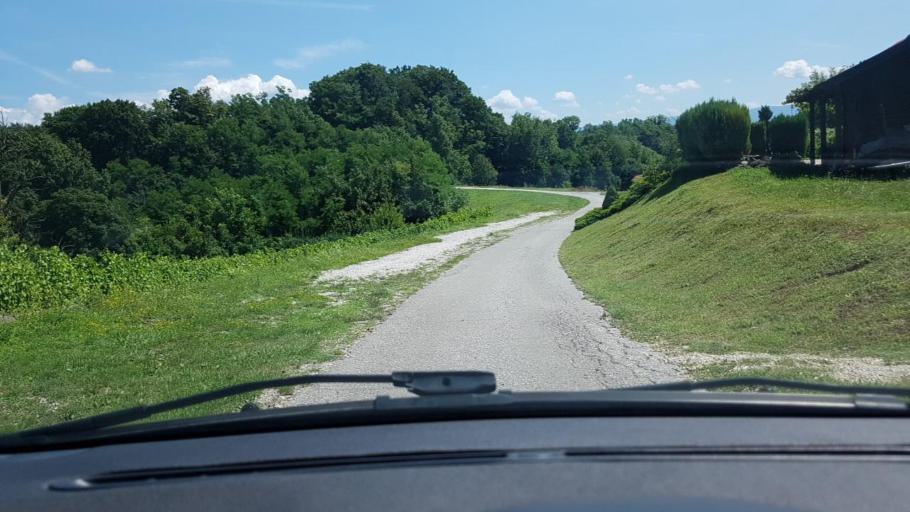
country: HR
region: Krapinsko-Zagorska
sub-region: Grad Krapina
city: Krapina
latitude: 46.1144
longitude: 15.8489
